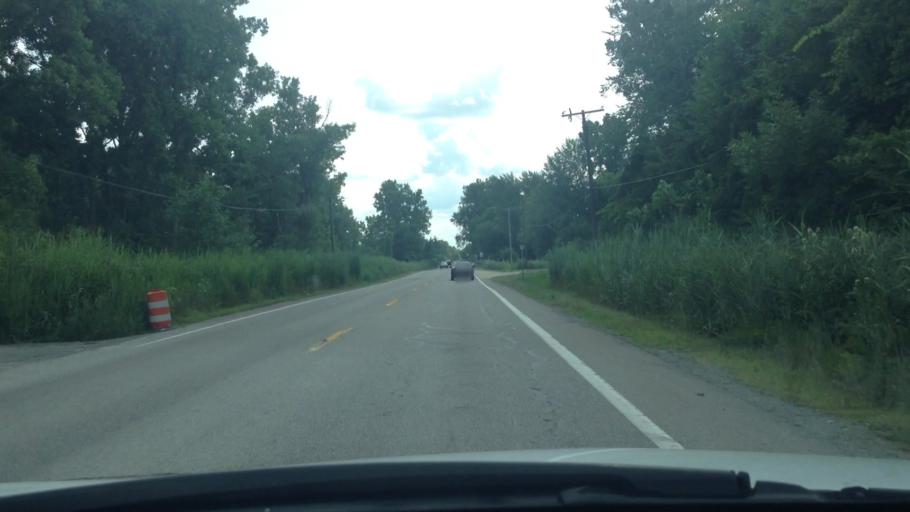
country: US
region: Michigan
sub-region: Wayne County
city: Taylor
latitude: 42.2015
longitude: -83.3068
